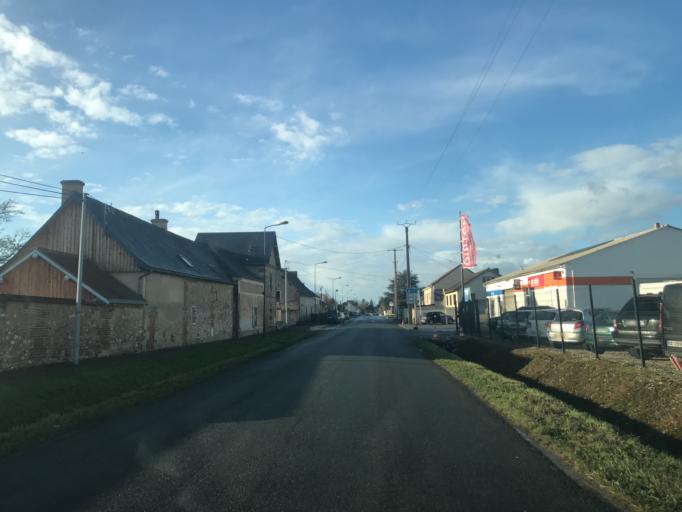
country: FR
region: Haute-Normandie
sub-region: Departement de l'Eure
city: Saint-Aubin-sur-Gaillon
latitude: 49.0941
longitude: 1.2837
